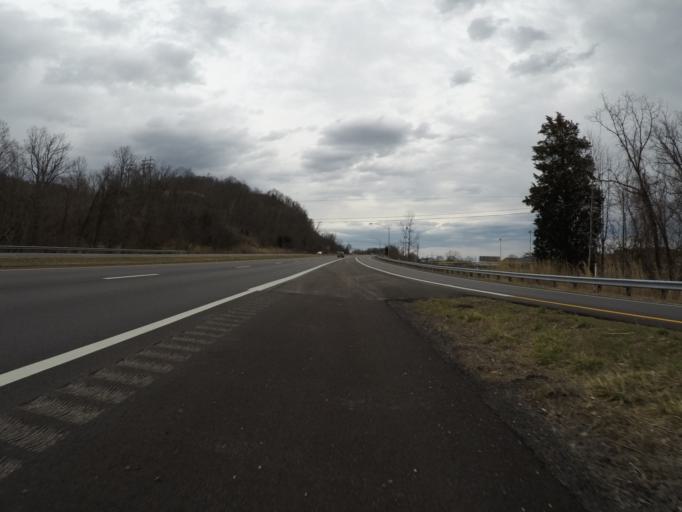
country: US
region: West Virginia
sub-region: Cabell County
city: Huntington
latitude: 38.4236
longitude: -82.4880
